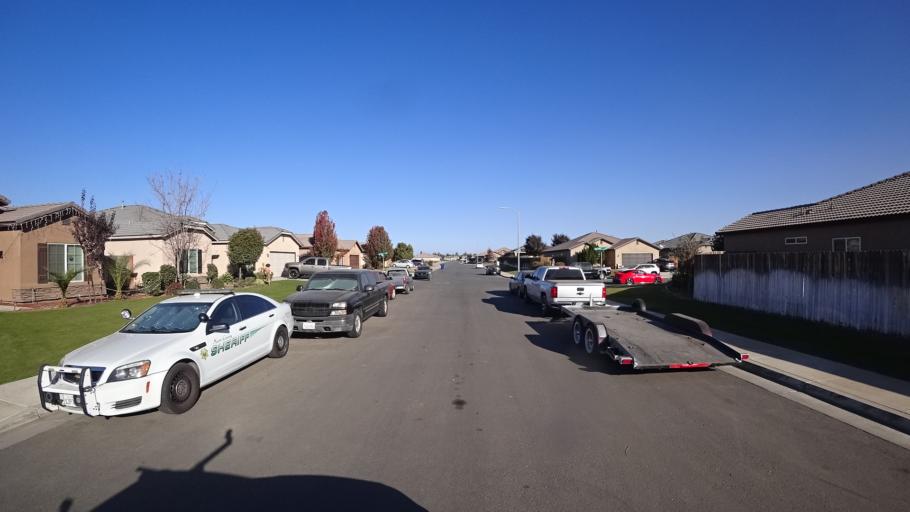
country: US
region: California
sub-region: Kern County
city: Greenfield
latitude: 35.2680
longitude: -119.0450
